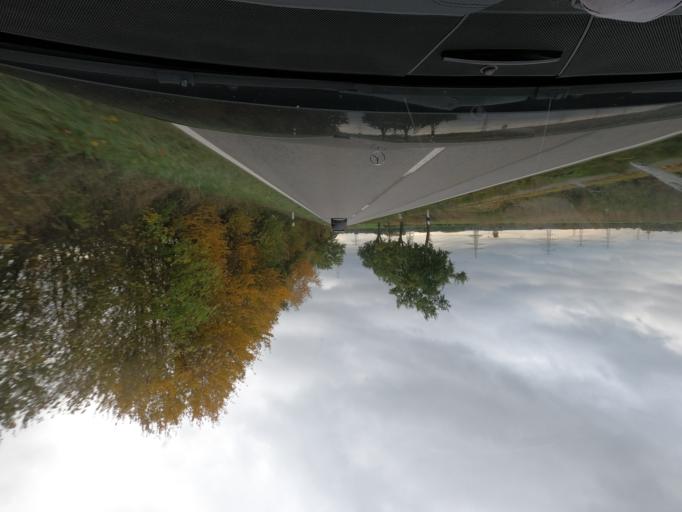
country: DE
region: Schleswig-Holstein
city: Hohenhorn
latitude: 53.4655
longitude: 10.3681
